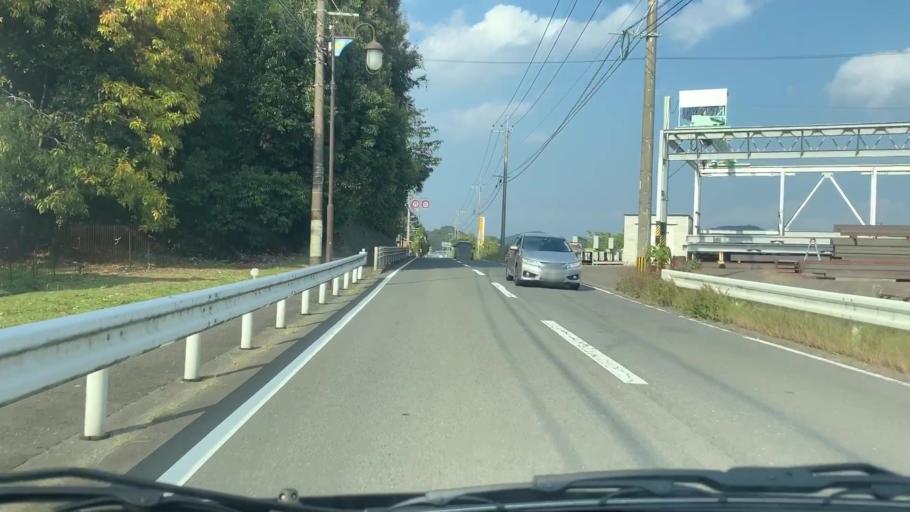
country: JP
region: Nagasaki
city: Togitsu
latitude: 32.9409
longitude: 129.7819
